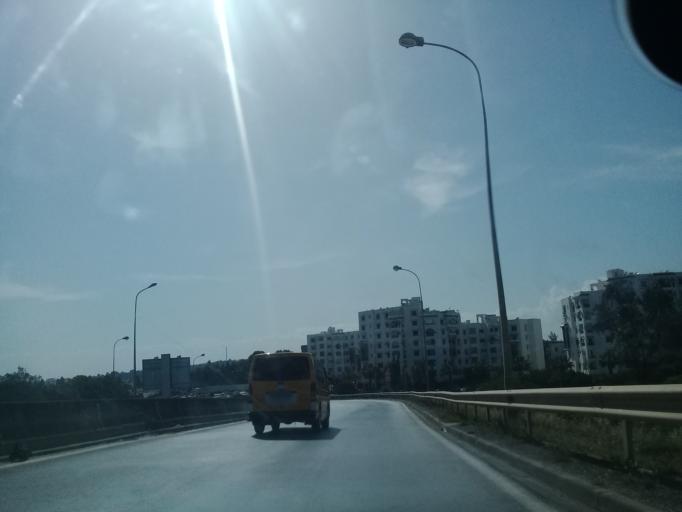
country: TN
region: Tunis
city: Tunis
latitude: 36.8249
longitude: 10.1992
